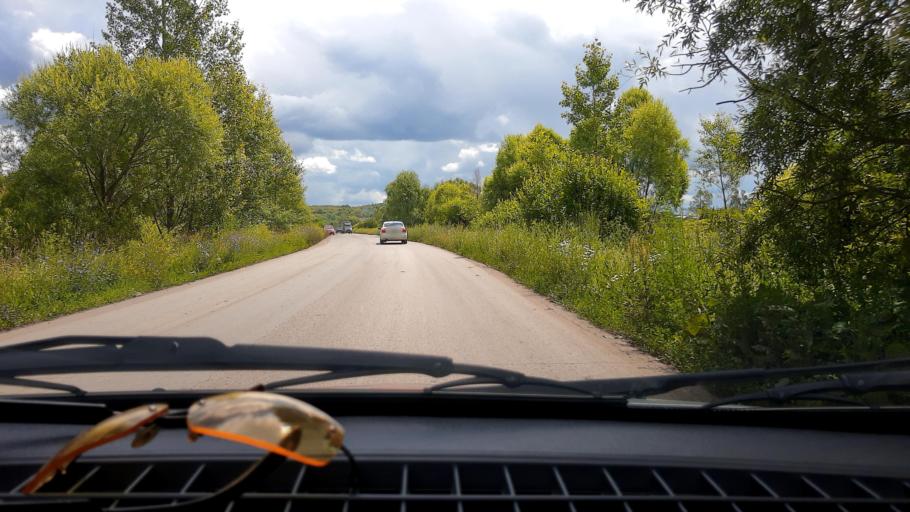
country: RU
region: Bashkortostan
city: Ufa
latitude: 54.7016
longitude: 56.1224
